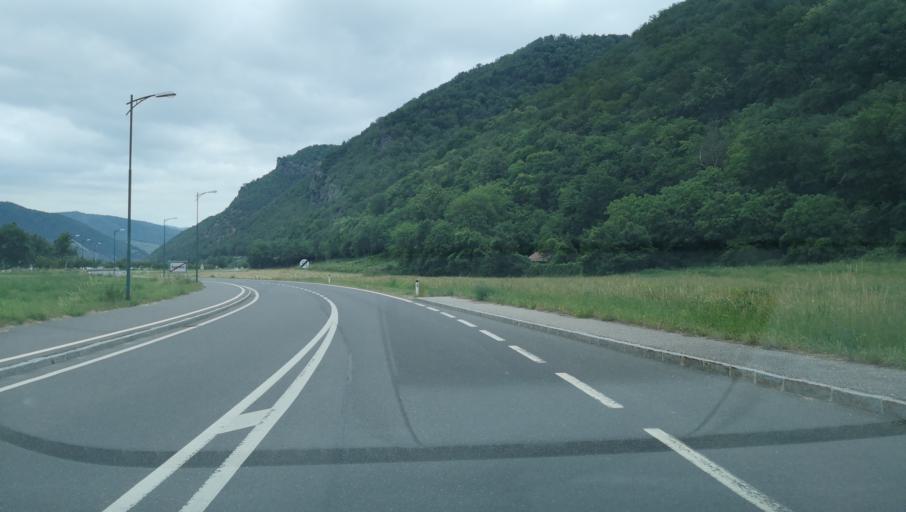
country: AT
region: Lower Austria
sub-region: Politischer Bezirk Krems
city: Aggsbach
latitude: 48.3105
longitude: 15.4134
